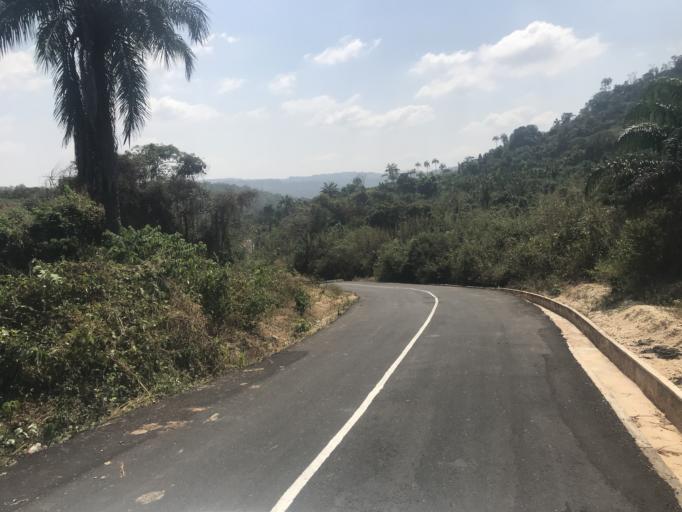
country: NG
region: Osun
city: Otan Ayegbaju
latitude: 7.9033
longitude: 4.8294
